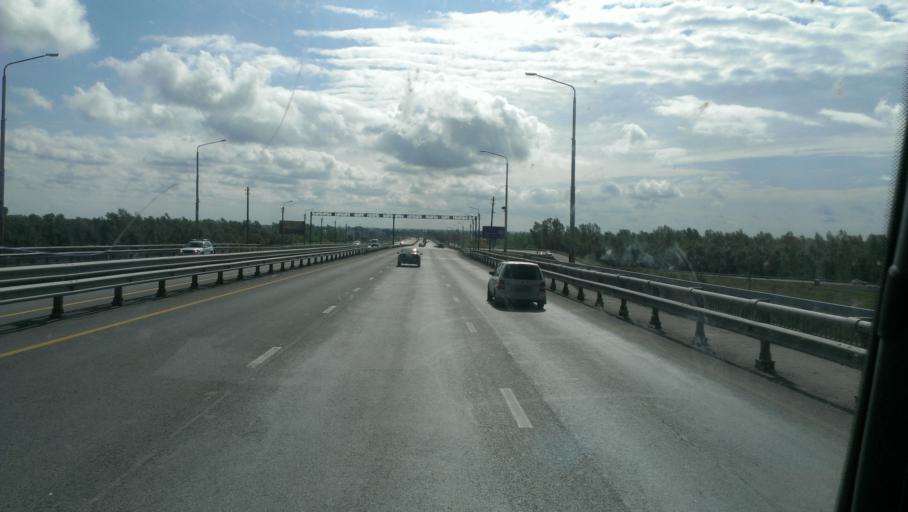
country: RU
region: Altai Krai
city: Zaton
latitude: 53.3210
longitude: 83.8101
